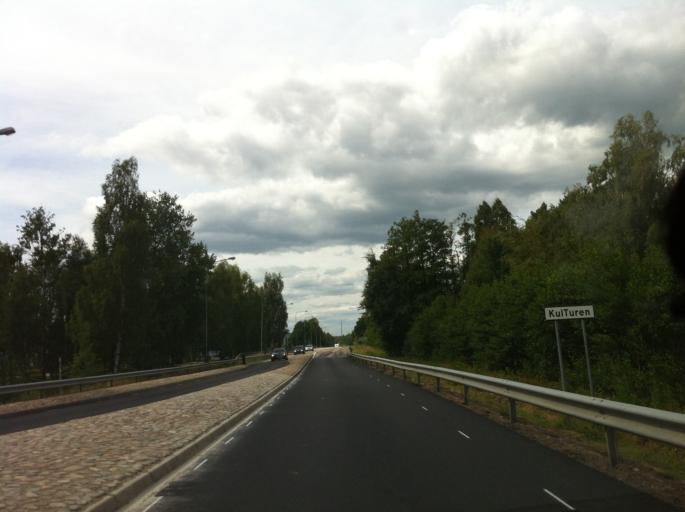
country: SE
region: Kalmar
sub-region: Emmaboda Kommun
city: Emmaboda
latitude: 56.6243
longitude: 15.5693
